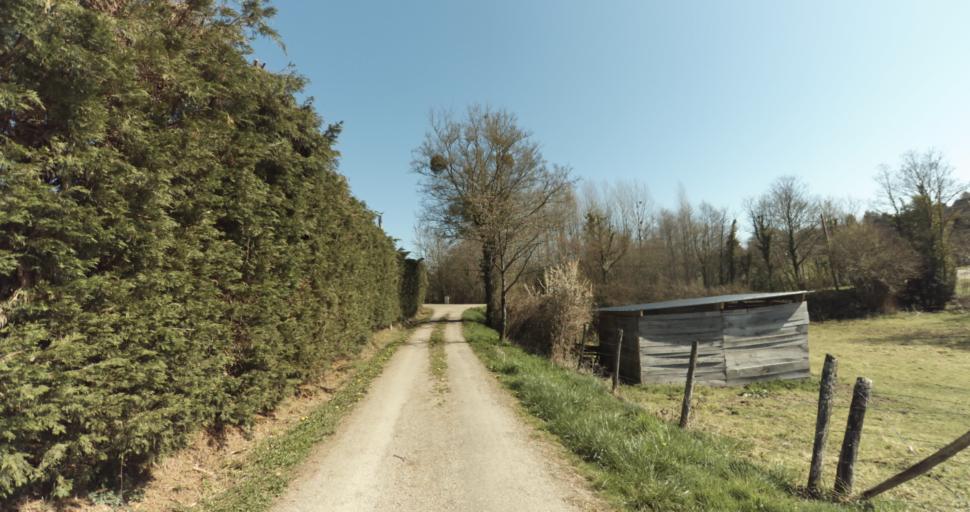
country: FR
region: Lower Normandy
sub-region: Departement du Calvados
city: Livarot
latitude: 49.0138
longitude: 0.0874
